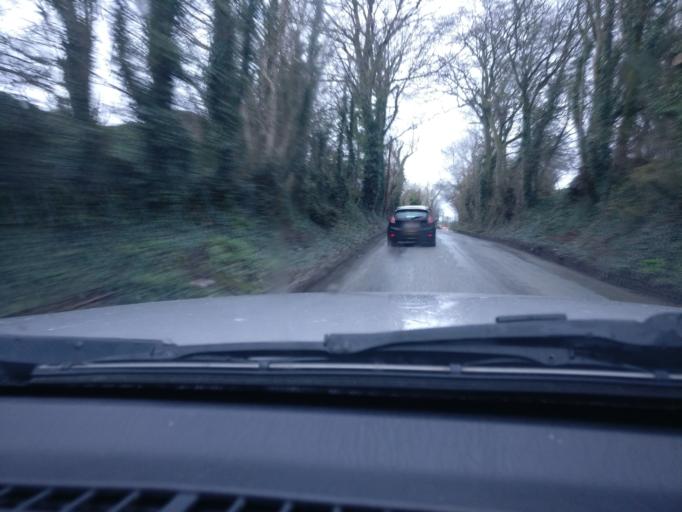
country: IE
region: Leinster
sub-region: An Mhi
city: Longwood
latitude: 53.4379
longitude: -6.9878
